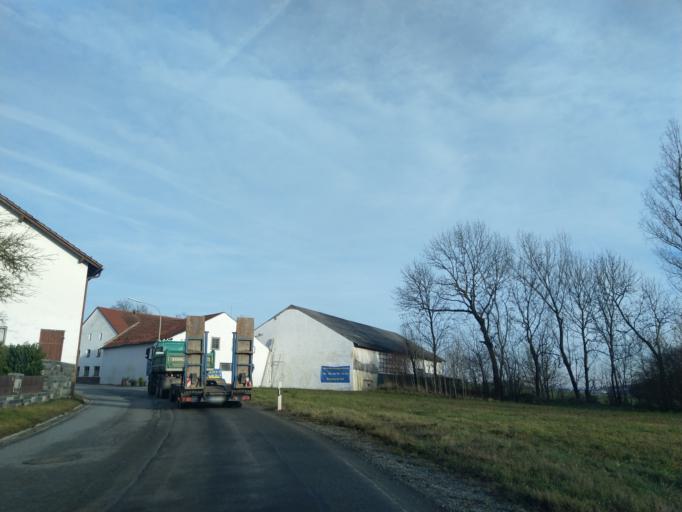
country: DE
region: Bavaria
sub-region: Lower Bavaria
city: Osterhofen
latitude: 48.7011
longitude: 12.9760
